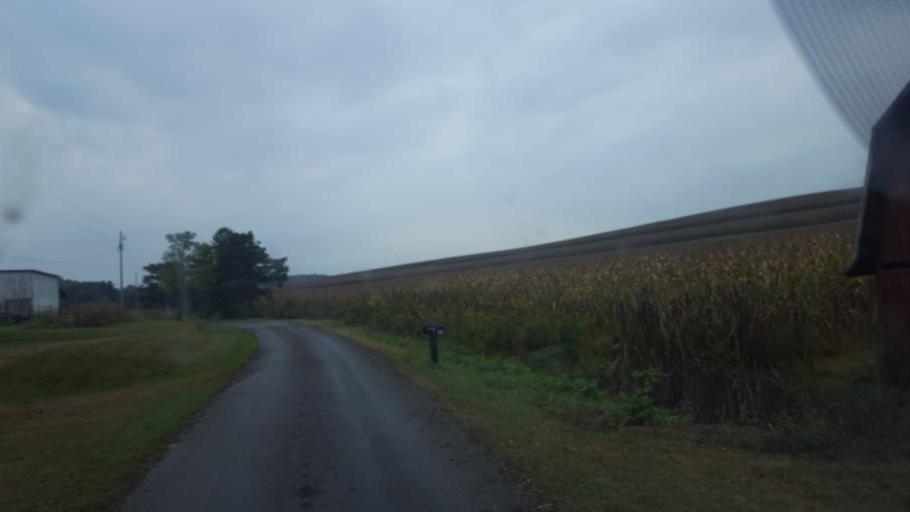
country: US
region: Ohio
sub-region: Ashland County
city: Loudonville
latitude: 40.5630
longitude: -82.2879
